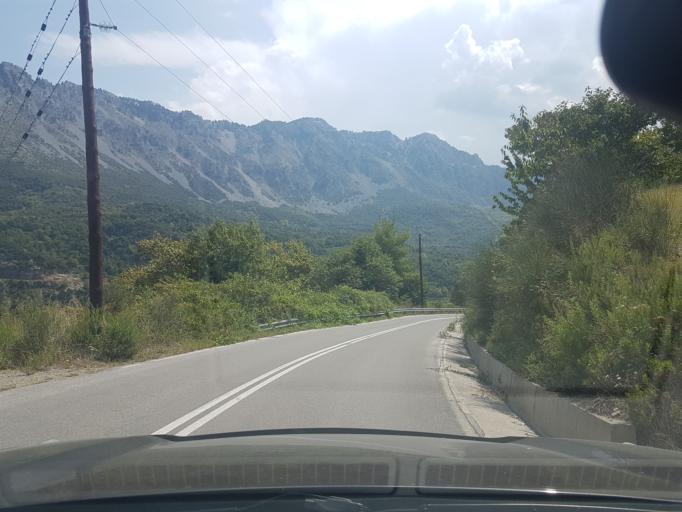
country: GR
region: Central Greece
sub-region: Nomos Evvoias
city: Kymi
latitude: 38.6350
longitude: 23.9452
